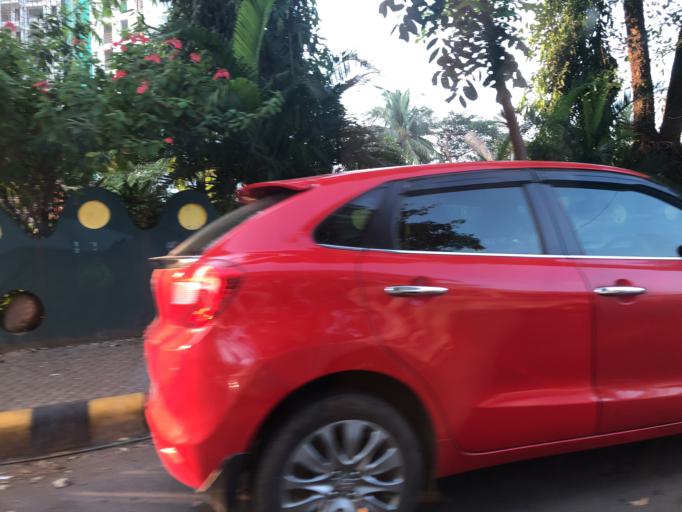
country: IN
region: Karnataka
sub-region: Dakshina Kannada
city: Mangalore
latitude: 12.8718
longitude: 74.8446
